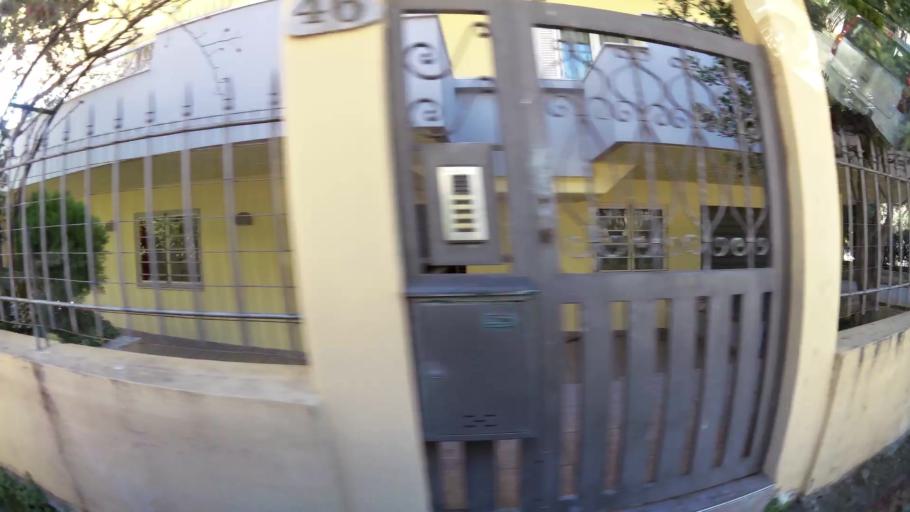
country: GR
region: Attica
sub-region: Nomarchia Athinas
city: Agia Paraskevi
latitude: 38.0196
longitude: 23.8419
